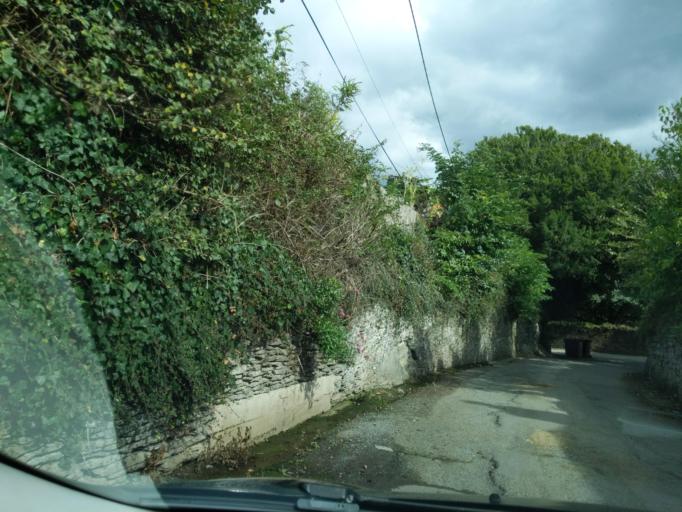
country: GB
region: England
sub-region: Plymouth
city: Plymstock
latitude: 50.3443
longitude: -4.0923
